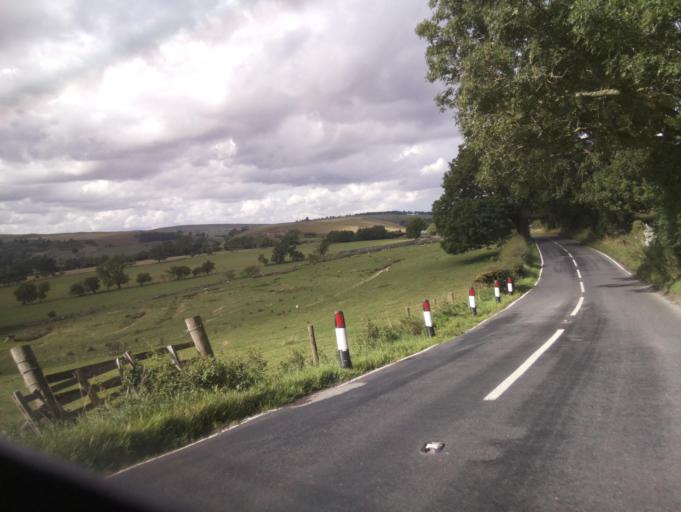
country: GB
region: England
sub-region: North Yorkshire
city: Leyburn
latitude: 54.3708
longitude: -1.8274
